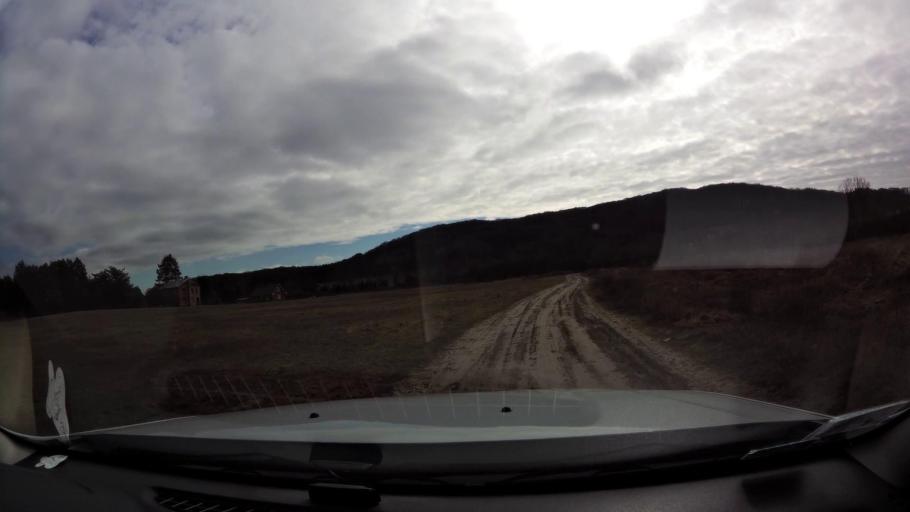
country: PL
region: West Pomeranian Voivodeship
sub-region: Powiat kamienski
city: Miedzyzdroje
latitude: 53.8816
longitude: 14.4480
